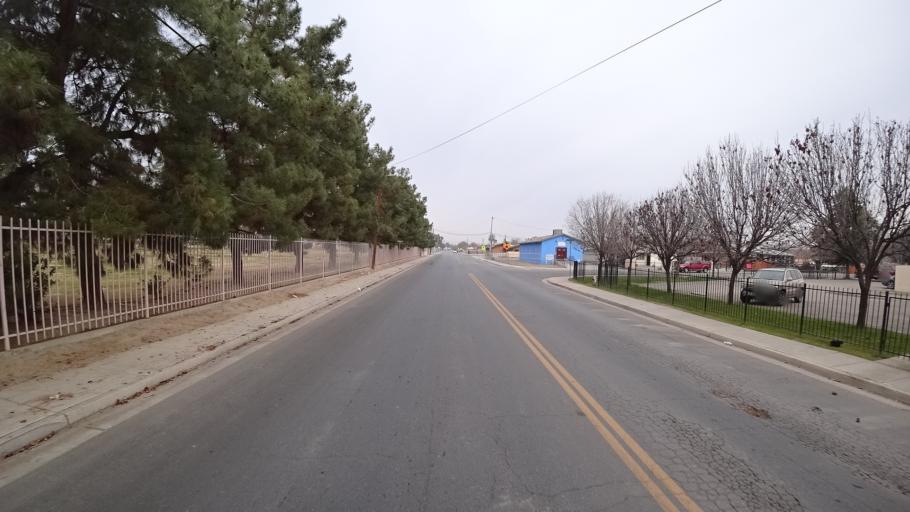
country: US
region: California
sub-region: Kern County
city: Bakersfield
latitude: 35.3636
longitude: -118.9909
